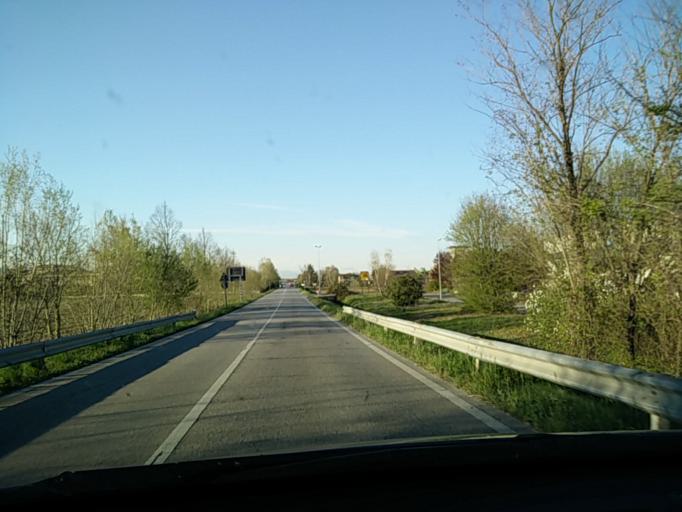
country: IT
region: Veneto
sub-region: Provincia di Venezia
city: Quarto d'Altino
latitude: 45.5827
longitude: 12.3752
